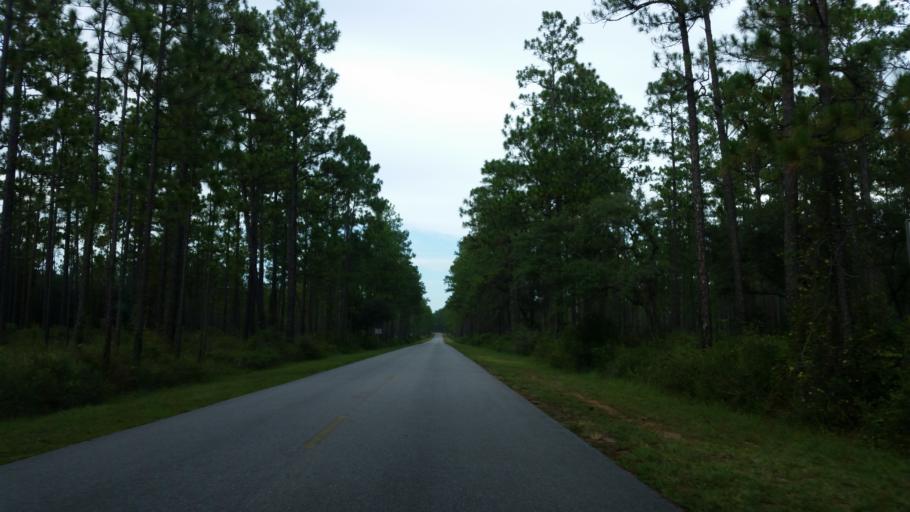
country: US
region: Florida
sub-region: Santa Rosa County
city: East Milton
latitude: 30.7136
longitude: -86.8790
